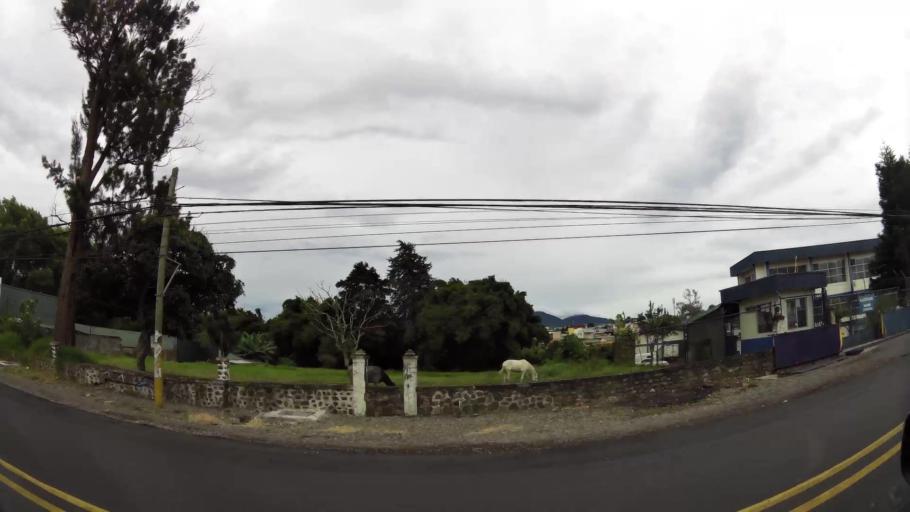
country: CR
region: San Jose
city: Ipis
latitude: 9.9684
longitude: -84.0200
